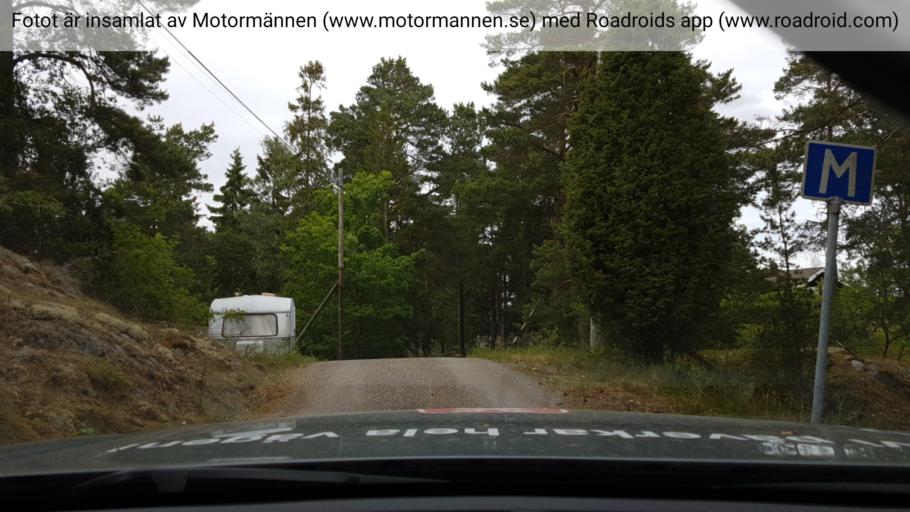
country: SE
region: Stockholm
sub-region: Haninge Kommun
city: Jordbro
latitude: 59.0227
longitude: 18.0996
